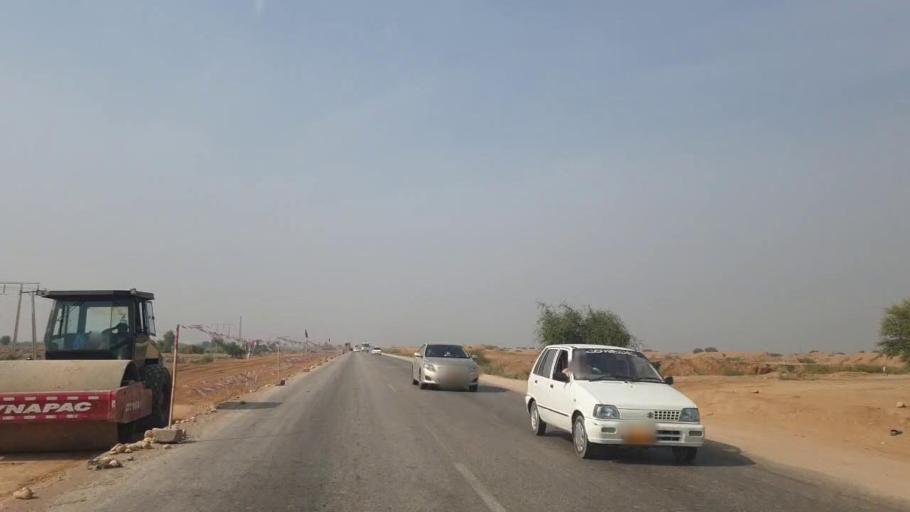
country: PK
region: Sindh
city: Sann
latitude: 26.1231
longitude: 68.0572
